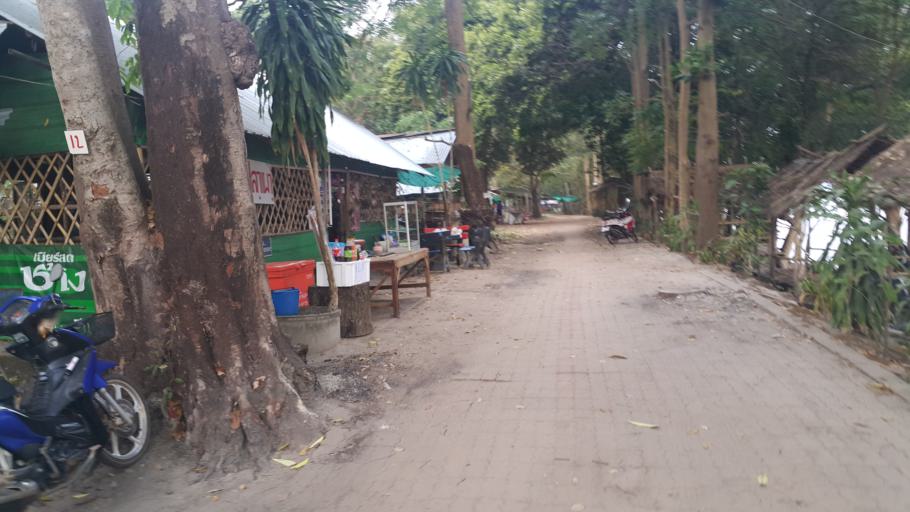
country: TH
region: Nong Khai
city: Bueng Khong Long
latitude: 17.9791
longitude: 104.0276
